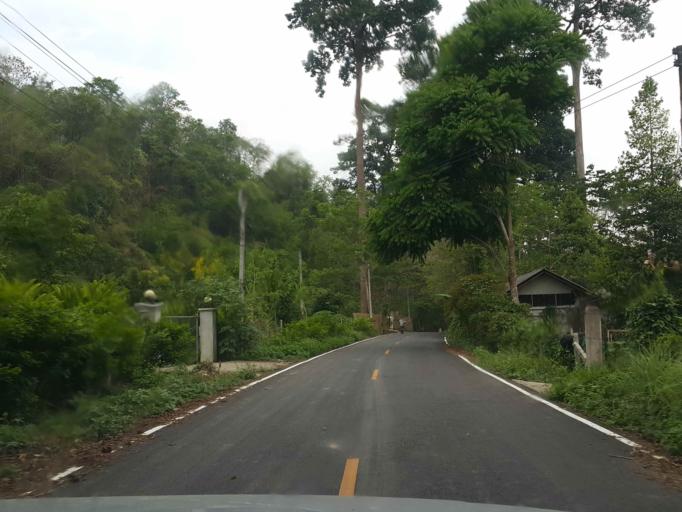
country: TH
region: Chiang Mai
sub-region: Amphoe Chiang Dao
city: Chiang Dao
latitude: 19.4057
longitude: 98.9267
